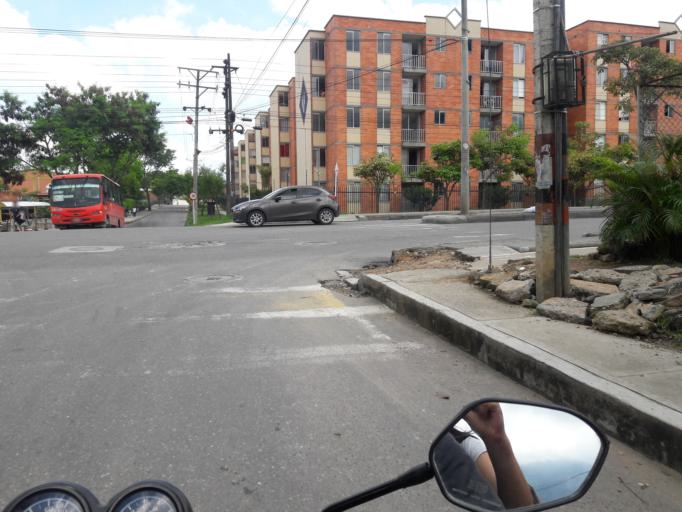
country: CO
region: Tolima
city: Ibague
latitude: 4.4462
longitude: -75.1598
